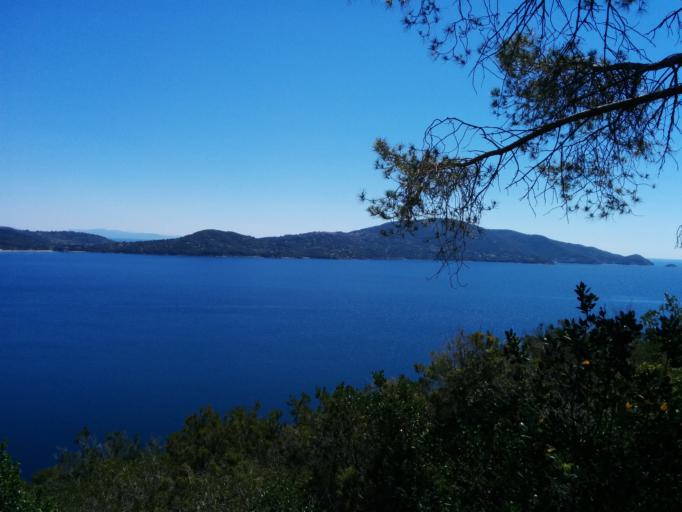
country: IT
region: Tuscany
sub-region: Provincia di Livorno
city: Capoliveri
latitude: 42.7520
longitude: 10.3193
